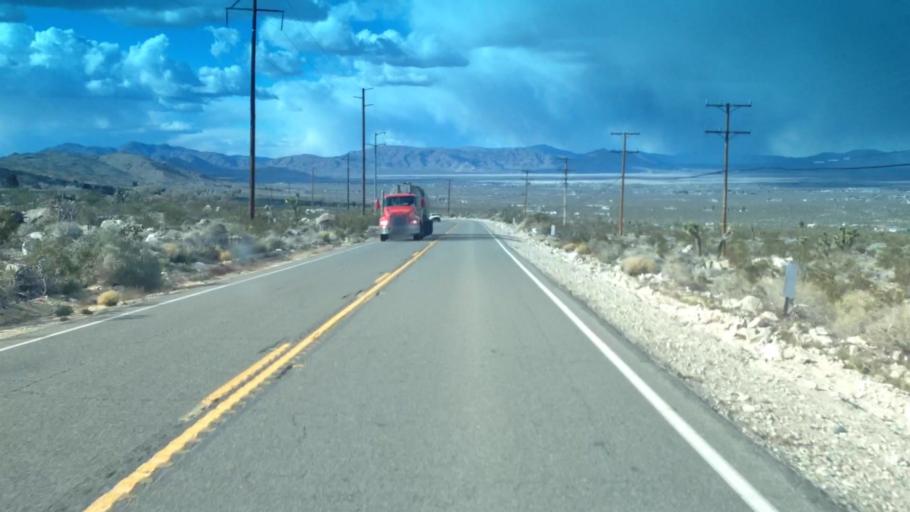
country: US
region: California
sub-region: San Bernardino County
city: Lucerne Valley
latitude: 34.3824
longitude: -116.8715
